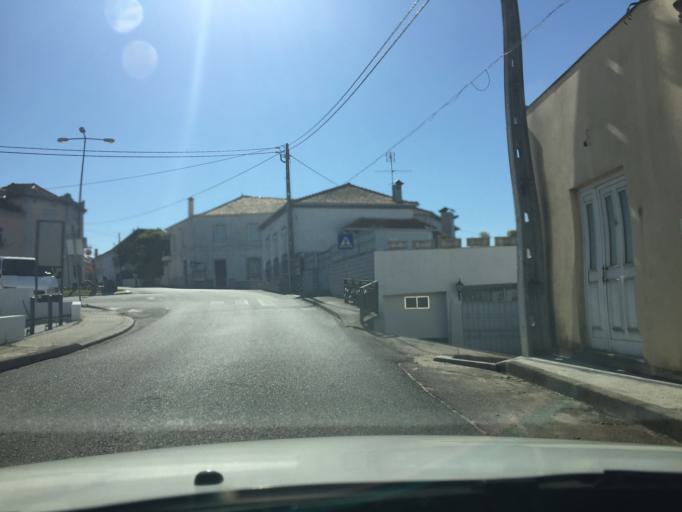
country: PT
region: Aveiro
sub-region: Oliveira do Bairro
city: Oliveira do Bairro
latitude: 40.4779
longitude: -8.5399
